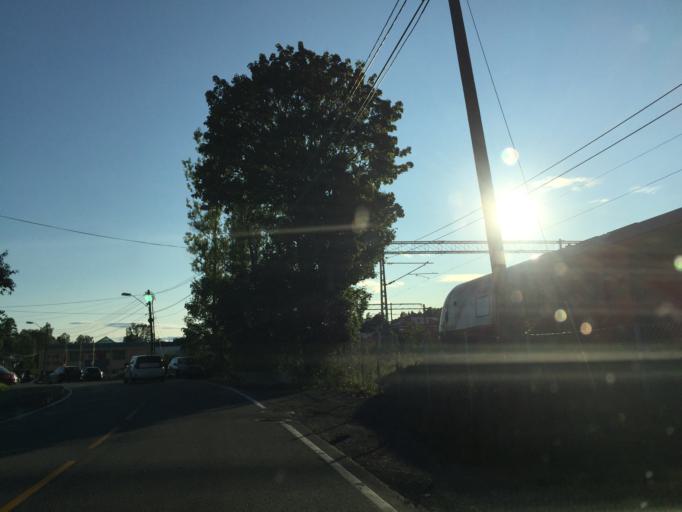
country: NO
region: Akershus
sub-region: Baerum
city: Lysaker
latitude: 59.9075
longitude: 10.6061
